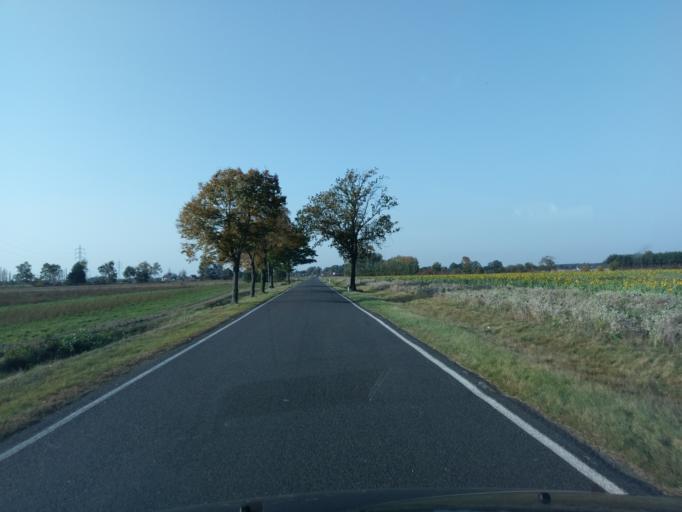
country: DE
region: Brandenburg
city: Falkenberg
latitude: 51.5601
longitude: 13.2608
